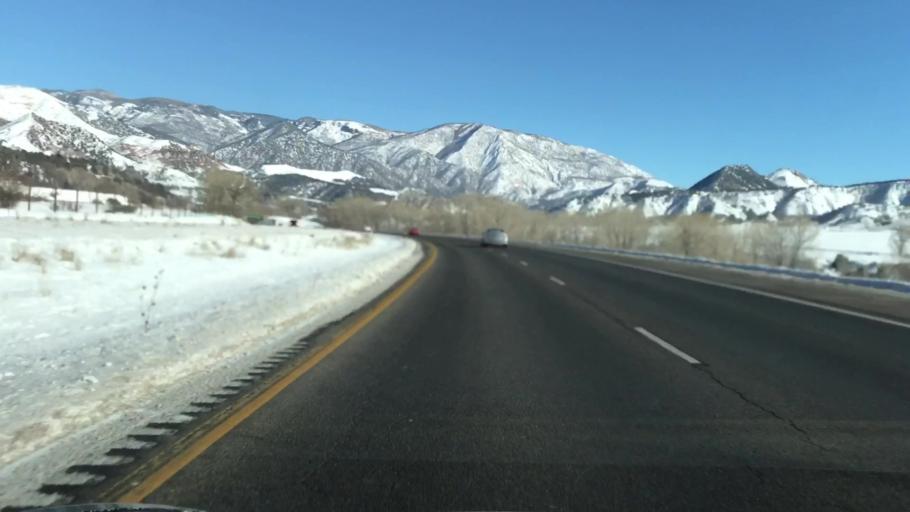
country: US
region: Colorado
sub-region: Garfield County
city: New Castle
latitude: 39.5657
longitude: -107.4913
